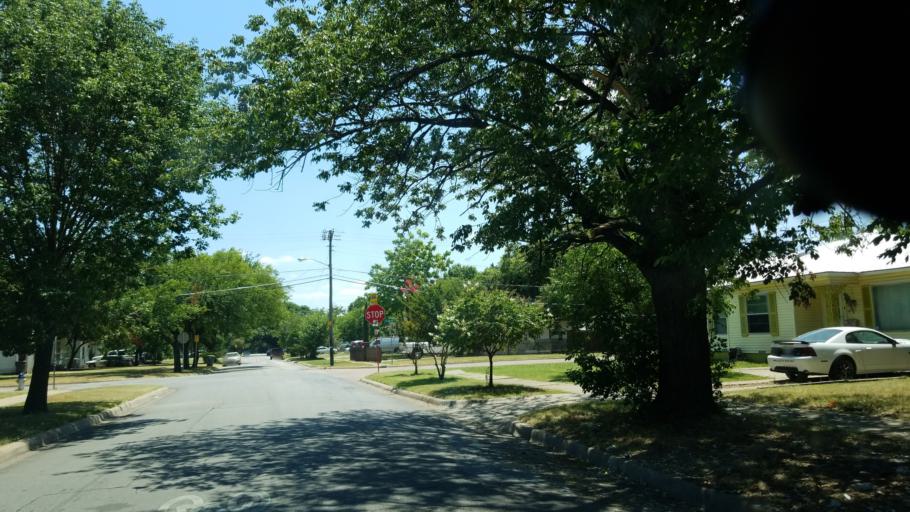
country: US
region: Texas
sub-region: Dallas County
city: Cockrell Hill
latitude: 32.7134
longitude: -96.8441
